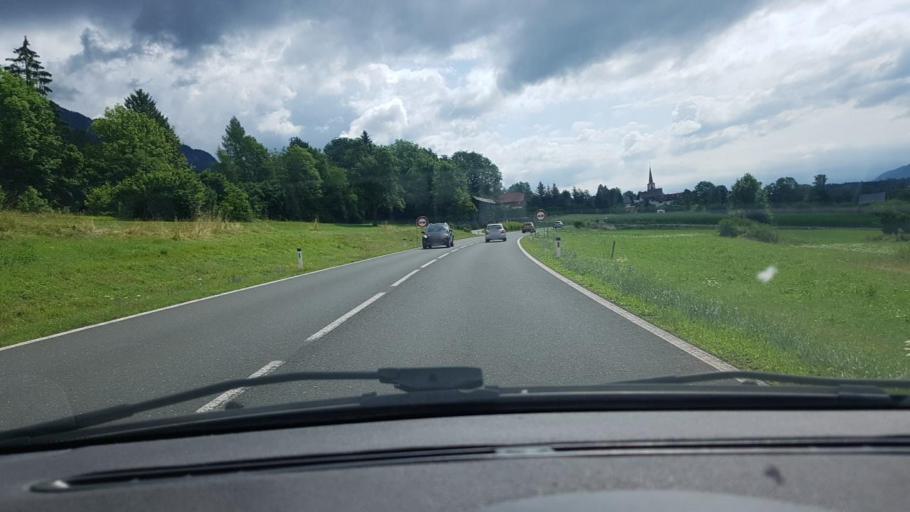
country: AT
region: Carinthia
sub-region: Politischer Bezirk Hermagor
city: Hermagor
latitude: 46.6317
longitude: 13.4643
